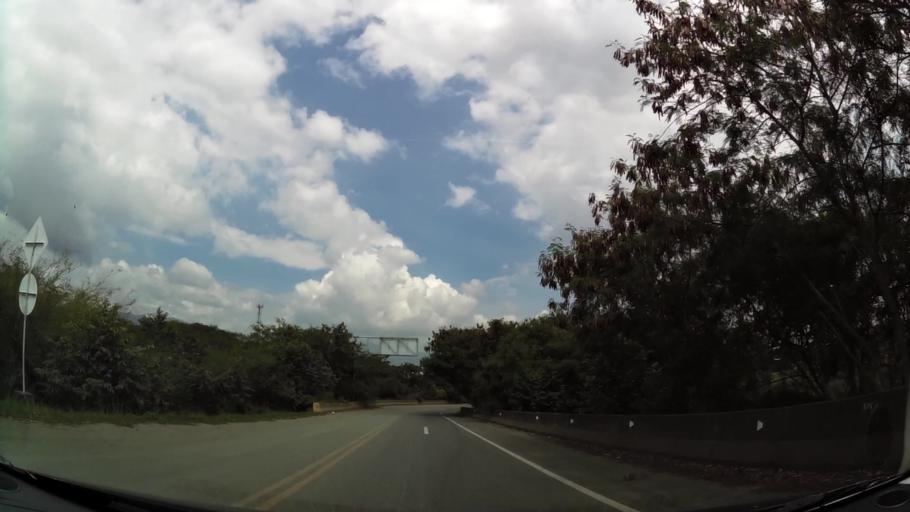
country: CO
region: Valle del Cauca
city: Cali
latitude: 3.4957
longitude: -76.4701
